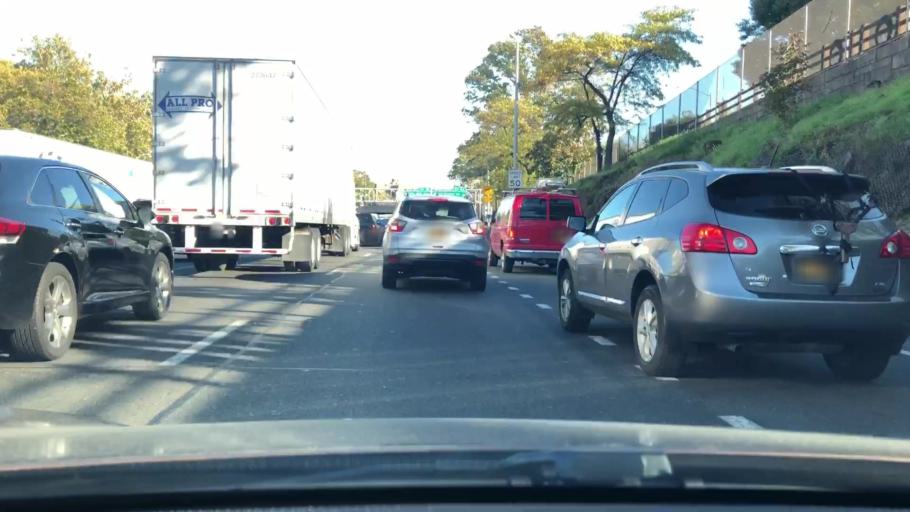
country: US
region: New York
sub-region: Bronx
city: The Bronx
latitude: 40.8357
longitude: -73.8692
